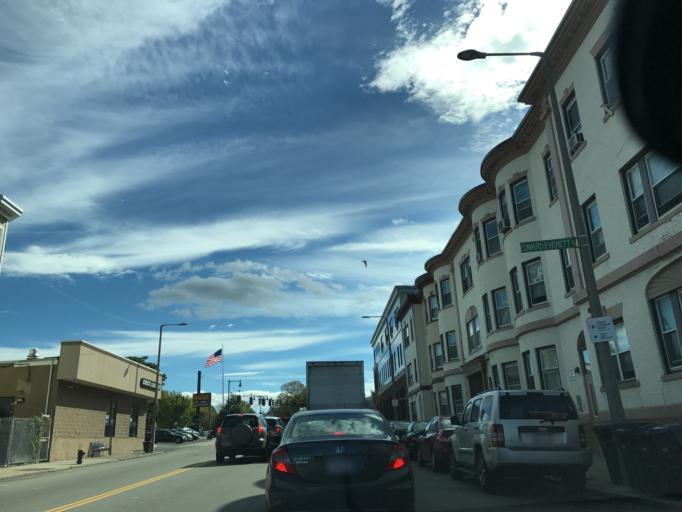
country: US
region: Massachusetts
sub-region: Suffolk County
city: South Boston
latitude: 42.3213
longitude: -71.0623
